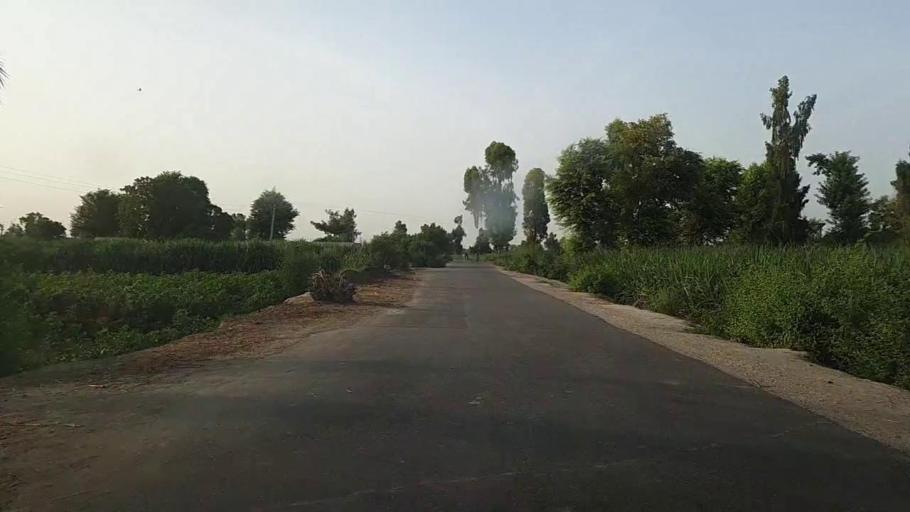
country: PK
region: Sindh
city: Ubauro
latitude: 28.1880
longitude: 69.8275
